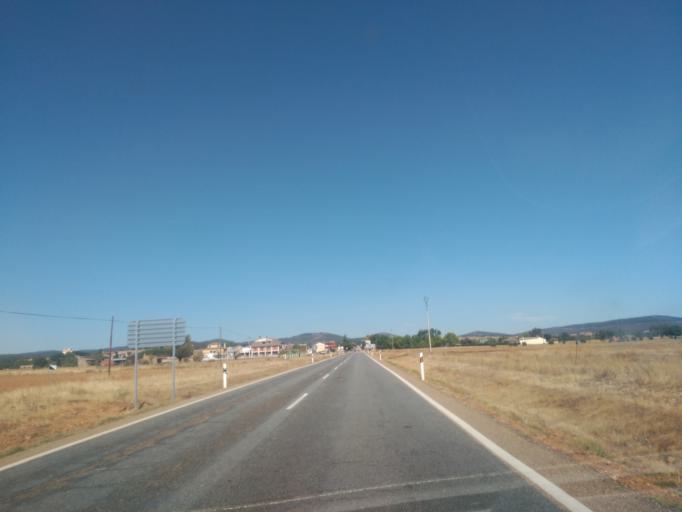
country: ES
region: Castille and Leon
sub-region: Provincia de Zamora
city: Tabara
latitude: 41.8184
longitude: -5.9461
